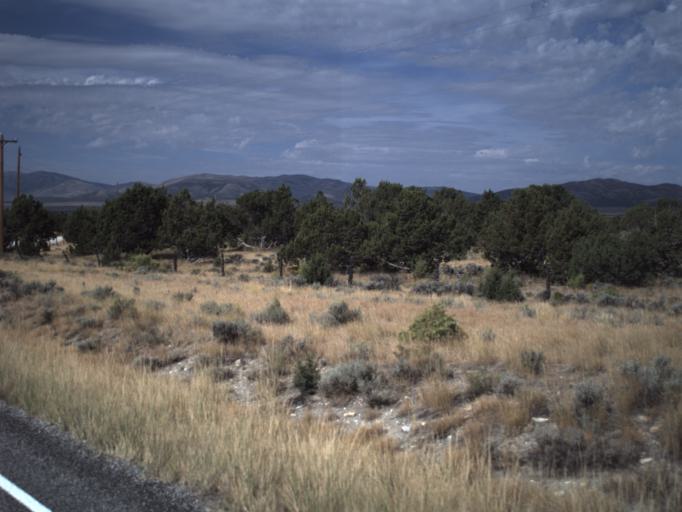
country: US
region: Idaho
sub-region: Cassia County
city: Burley
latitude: 41.8166
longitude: -113.4340
